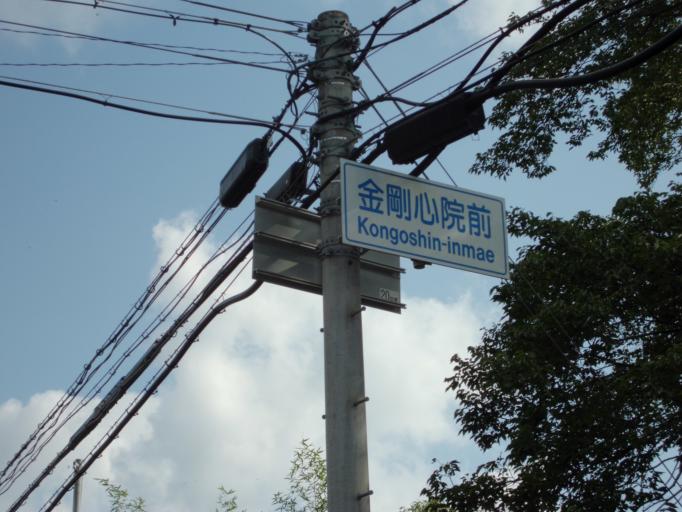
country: JP
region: Kyoto
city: Miyazu
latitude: 35.6095
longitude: 135.2213
